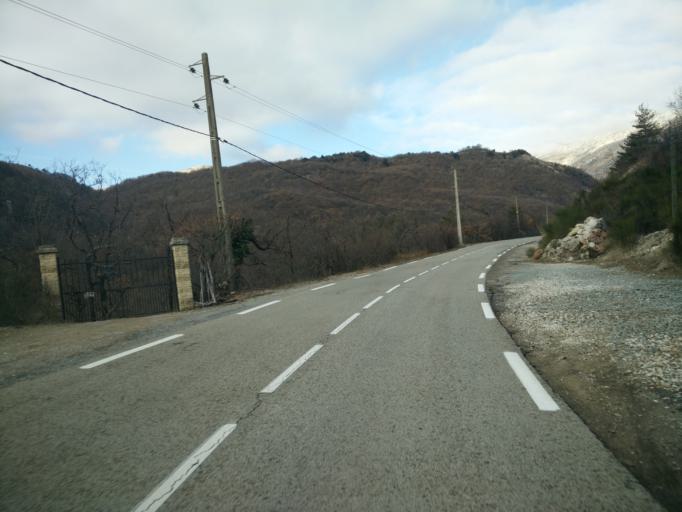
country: FR
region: Provence-Alpes-Cote d'Azur
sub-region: Departement des Alpes-Maritimes
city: Tourrettes-sur-Loup
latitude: 43.7755
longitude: 6.9814
